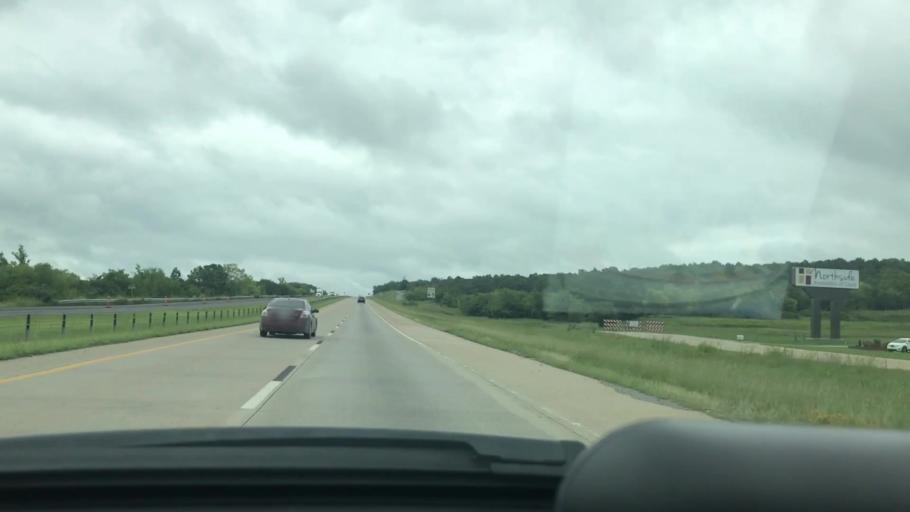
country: US
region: Oklahoma
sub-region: Pittsburg County
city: Krebs
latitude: 34.9612
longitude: -95.7247
